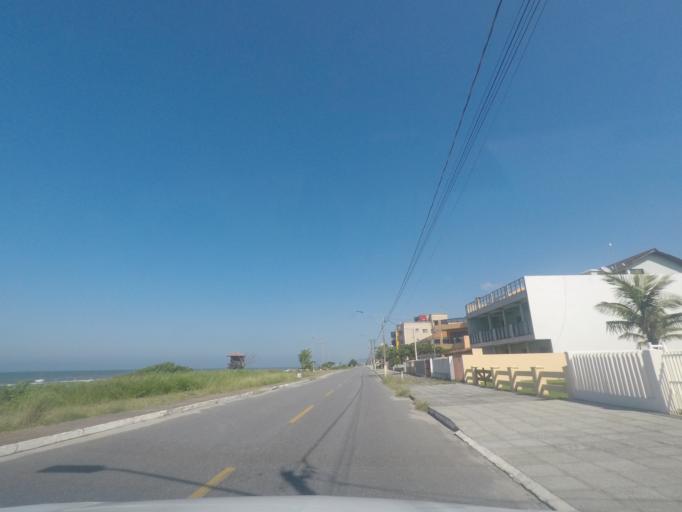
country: BR
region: Parana
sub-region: Pontal Do Parana
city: Pontal do Parana
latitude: -25.7602
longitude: -48.5062
